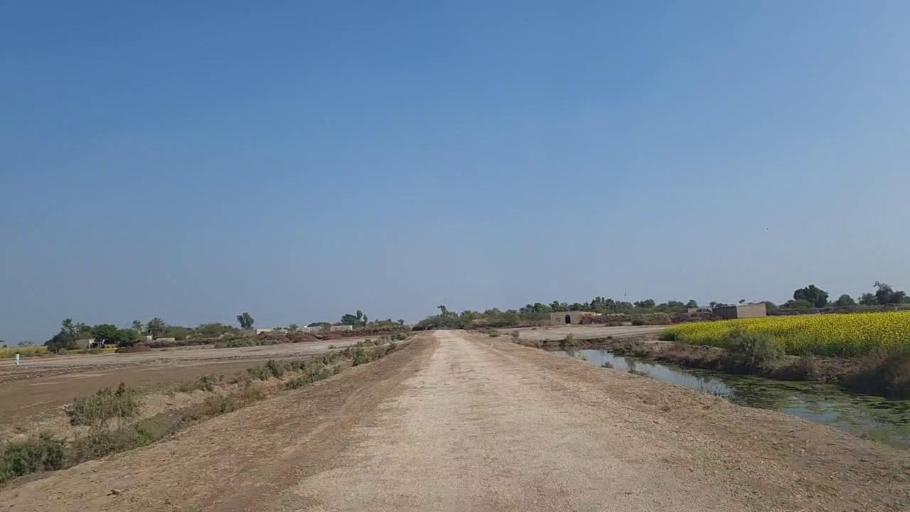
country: PK
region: Sindh
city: Jam Sahib
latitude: 26.2550
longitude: 68.5750
